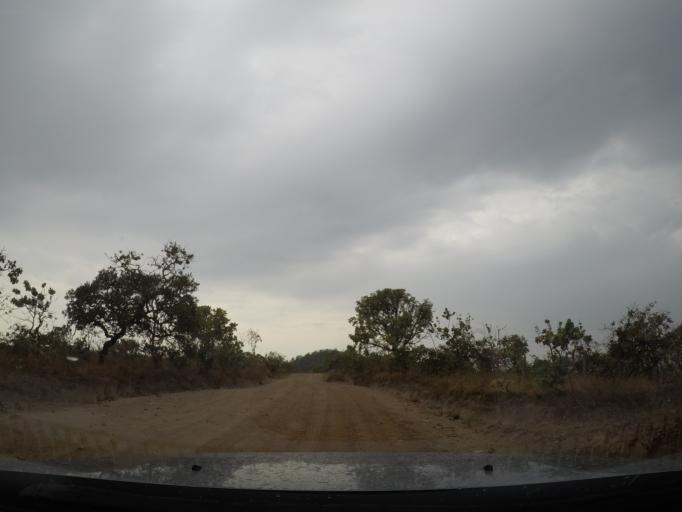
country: BR
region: Goias
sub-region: Pirenopolis
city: Pirenopolis
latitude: -15.8212
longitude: -48.9062
